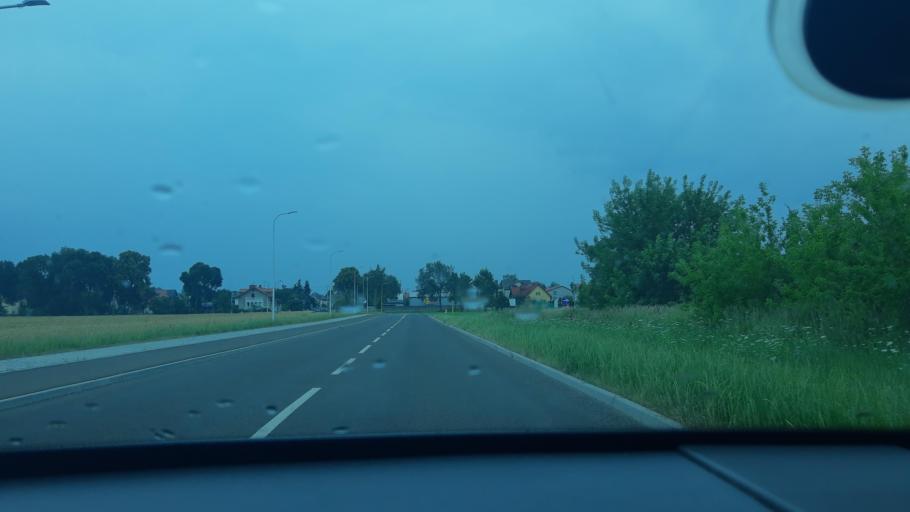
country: PL
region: Lodz Voivodeship
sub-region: Powiat sieradzki
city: Sieradz
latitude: 51.5723
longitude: 18.7020
